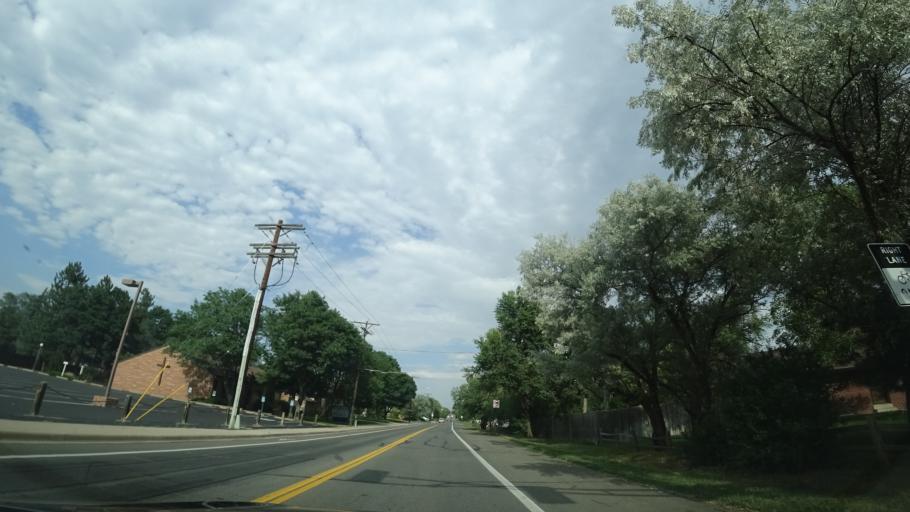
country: US
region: Colorado
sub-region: Jefferson County
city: Lakewood
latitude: 39.7185
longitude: -105.0908
